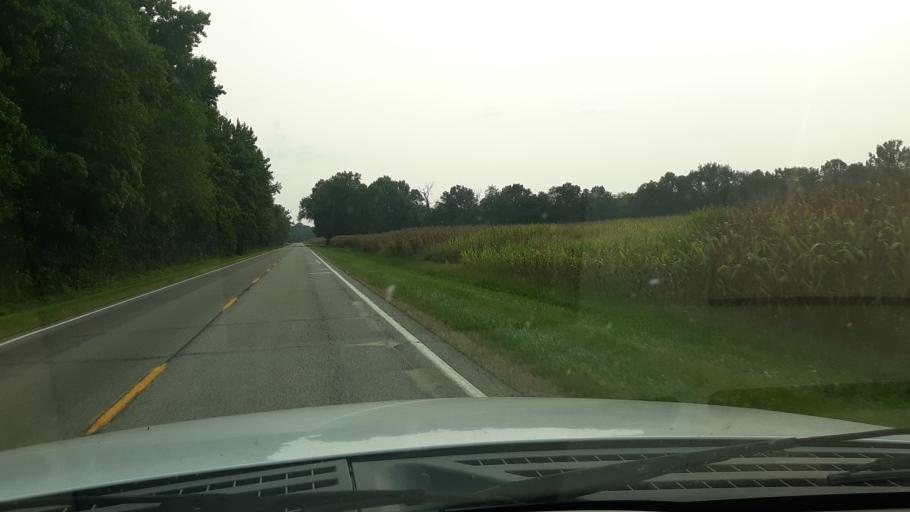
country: US
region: Illinois
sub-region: Edwards County
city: Grayville
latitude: 38.3040
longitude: -87.9472
